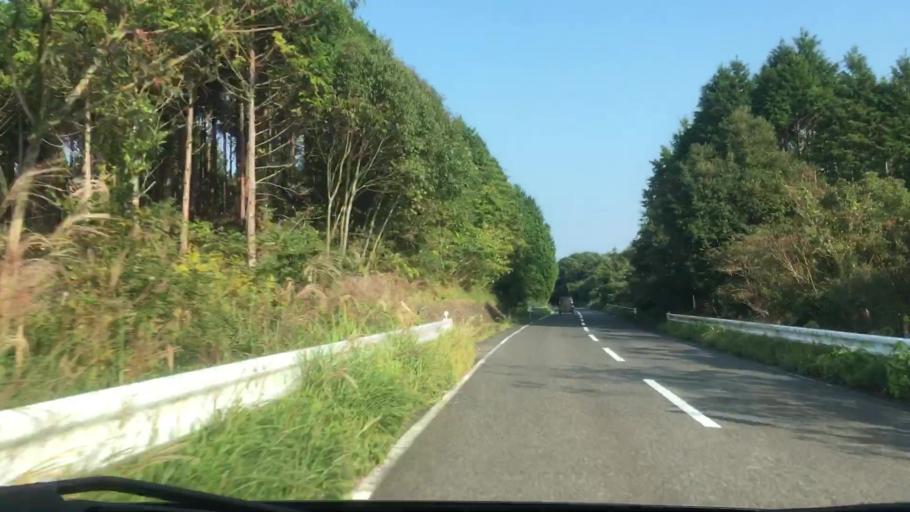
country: JP
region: Nagasaki
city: Sasebo
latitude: 33.0292
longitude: 129.6901
